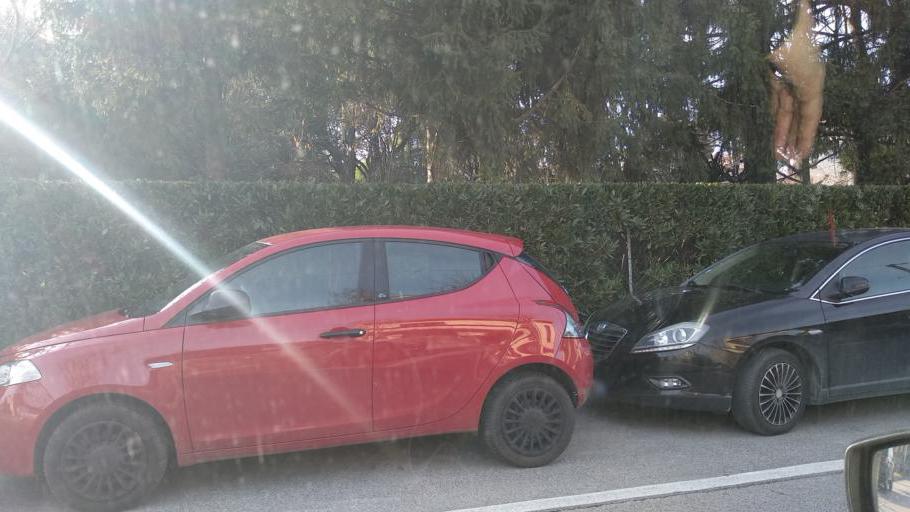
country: IT
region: Veneto
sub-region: Provincia di Treviso
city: Carpesica
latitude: 45.9513
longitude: 12.2907
